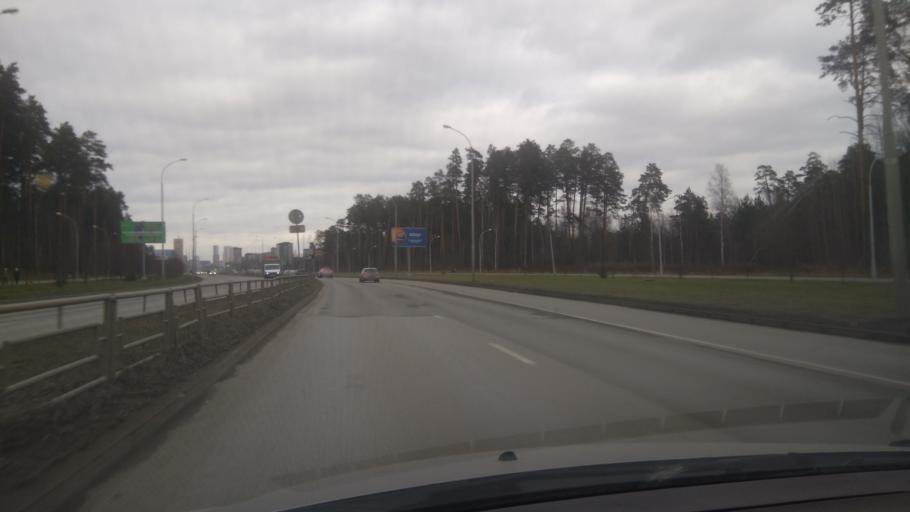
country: RU
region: Sverdlovsk
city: Sovkhoznyy
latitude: 56.7990
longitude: 60.5324
